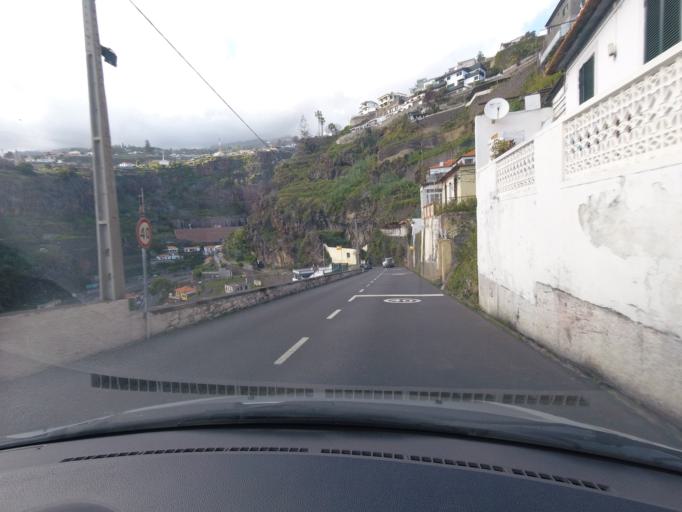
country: PT
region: Madeira
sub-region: Funchal
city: Nossa Senhora do Monte
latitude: 32.6583
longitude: -16.8993
